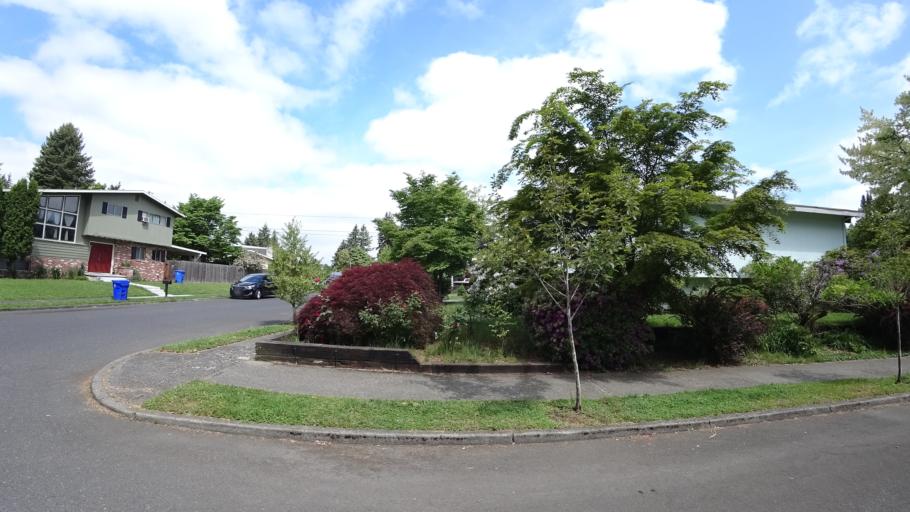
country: US
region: Oregon
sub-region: Multnomah County
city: Gresham
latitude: 45.4993
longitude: -122.4887
